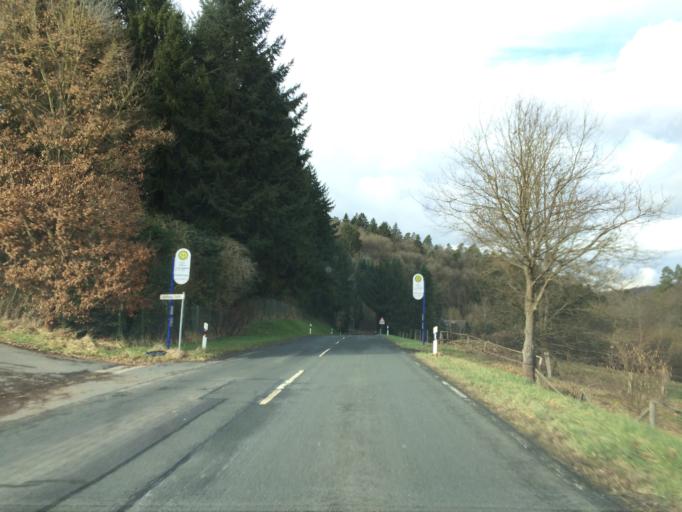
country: DE
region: Hesse
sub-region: Regierungsbezirk Darmstadt
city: Gravenwiesbach
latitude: 50.3626
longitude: 8.4001
